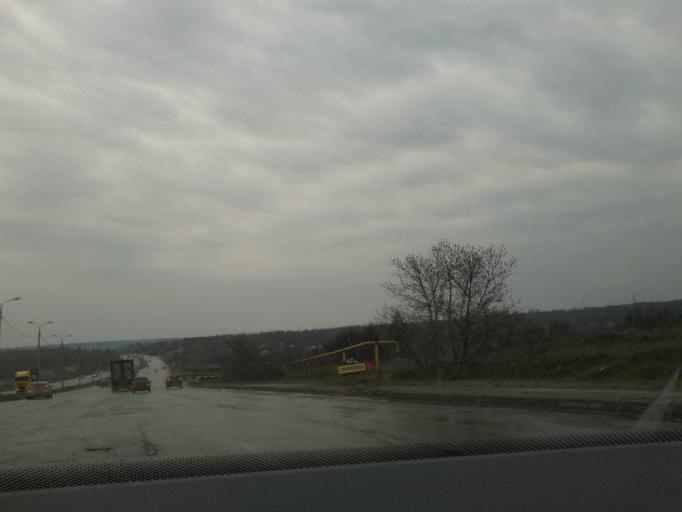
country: RU
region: Volgograd
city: Volgograd
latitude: 48.7345
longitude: 44.4562
